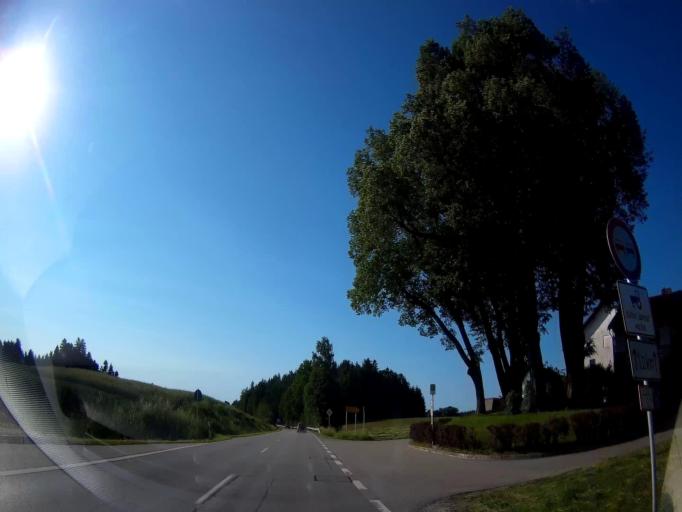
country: DE
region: Bavaria
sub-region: Lower Bavaria
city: Wurmannsquick
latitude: 48.3426
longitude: 12.8172
